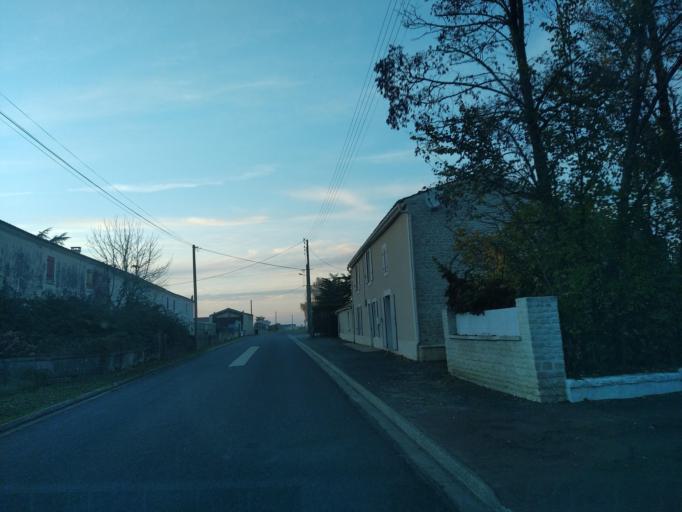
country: FR
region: Pays de la Loire
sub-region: Departement de la Vendee
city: Vix
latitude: 46.3992
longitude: -0.8455
